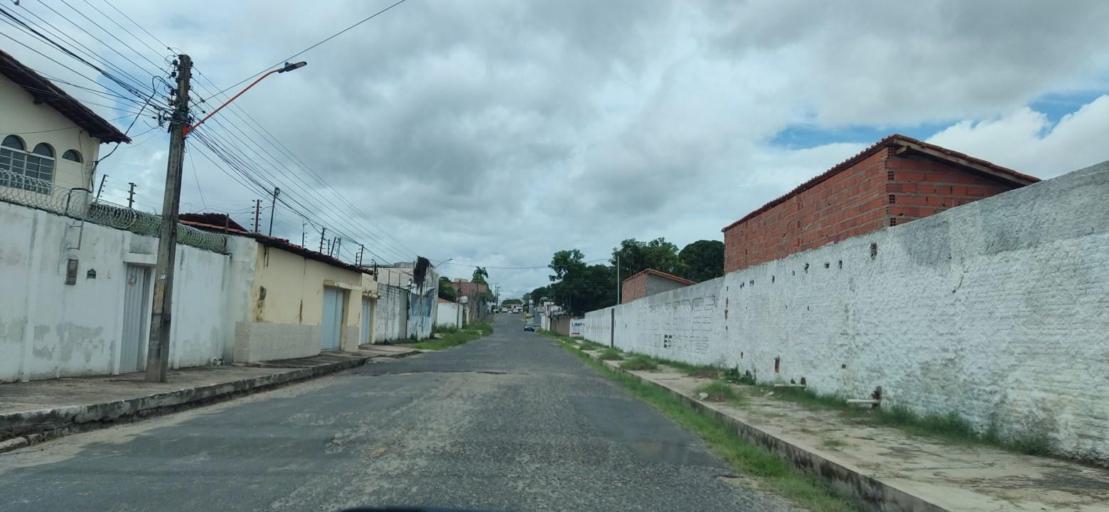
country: BR
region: Piaui
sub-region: Teresina
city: Teresina
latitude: -5.0741
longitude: -42.7684
